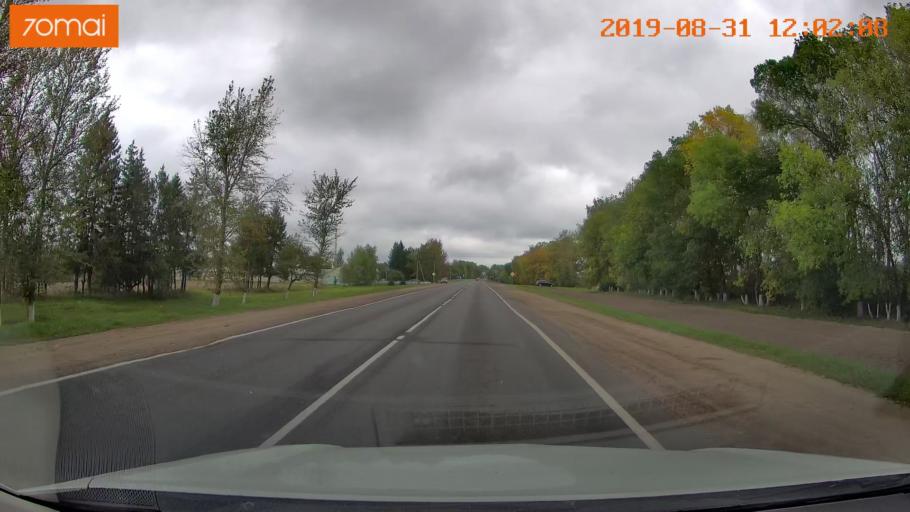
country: BY
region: Mogilev
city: Horad Krychaw
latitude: 53.6940
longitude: 31.6936
